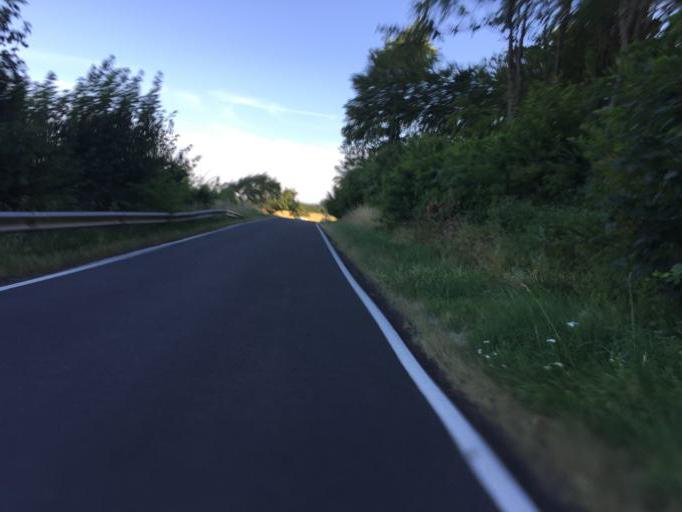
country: DE
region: Rheinland-Pfalz
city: Meudt
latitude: 50.5058
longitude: 7.8955
